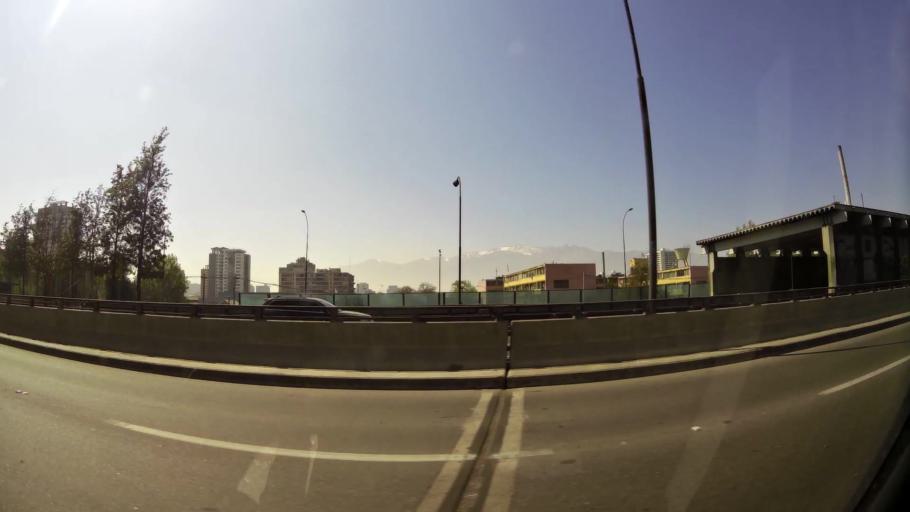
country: CL
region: Santiago Metropolitan
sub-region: Provincia de Santiago
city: Santiago
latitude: -33.4608
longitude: -70.6572
